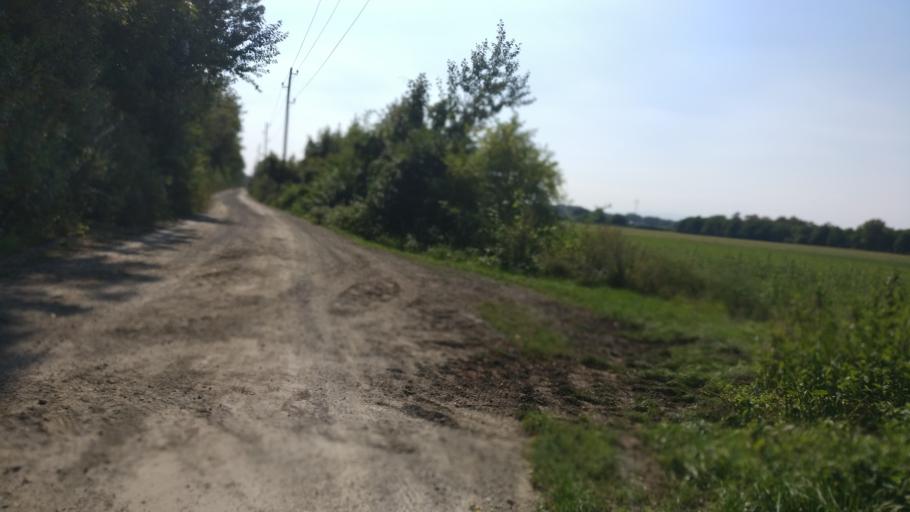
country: AT
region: Lower Austria
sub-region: Politischer Bezirk Baden
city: Ebreichsdorf
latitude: 47.9820
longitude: 16.4059
